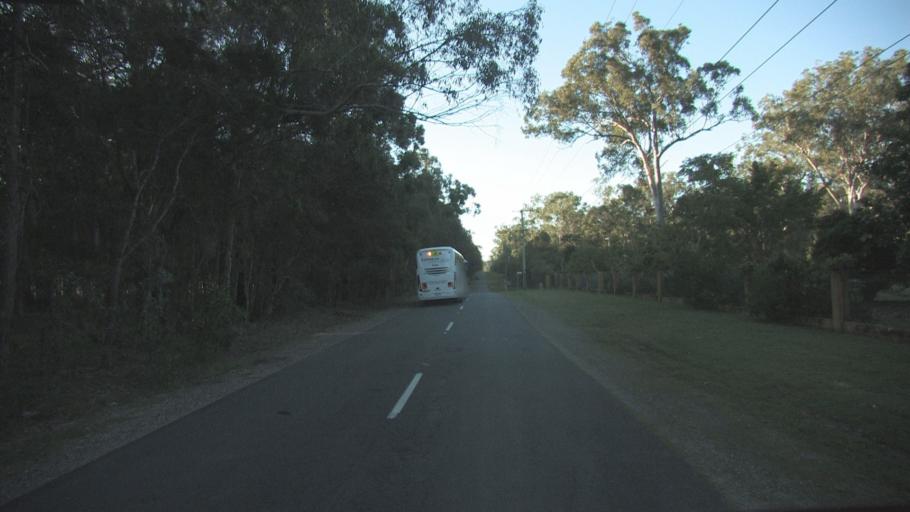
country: AU
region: Queensland
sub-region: Gold Coast
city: Yatala
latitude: -27.6837
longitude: 153.2746
